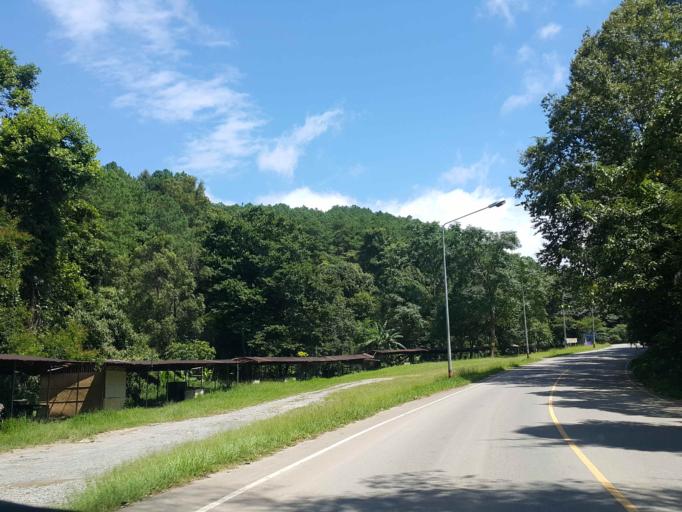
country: TH
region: Chiang Mai
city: Mae Chaem
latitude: 18.5292
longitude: 98.5230
